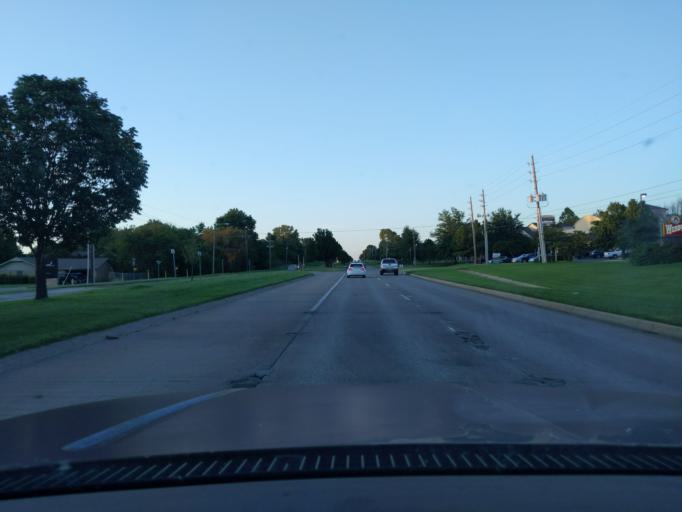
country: US
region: Oklahoma
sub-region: Tulsa County
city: Jenks
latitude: 36.0477
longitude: -95.8861
